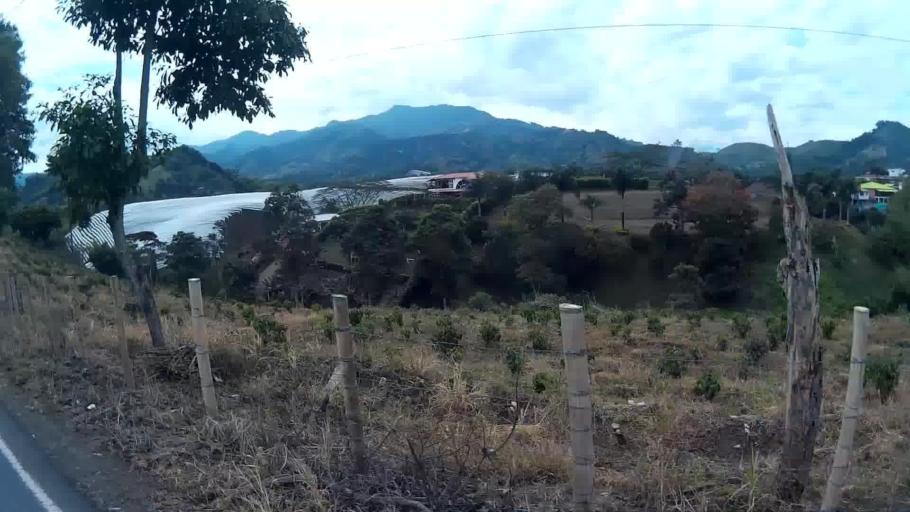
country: CO
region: Risaralda
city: Pereira
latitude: 4.8377
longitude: -75.7570
